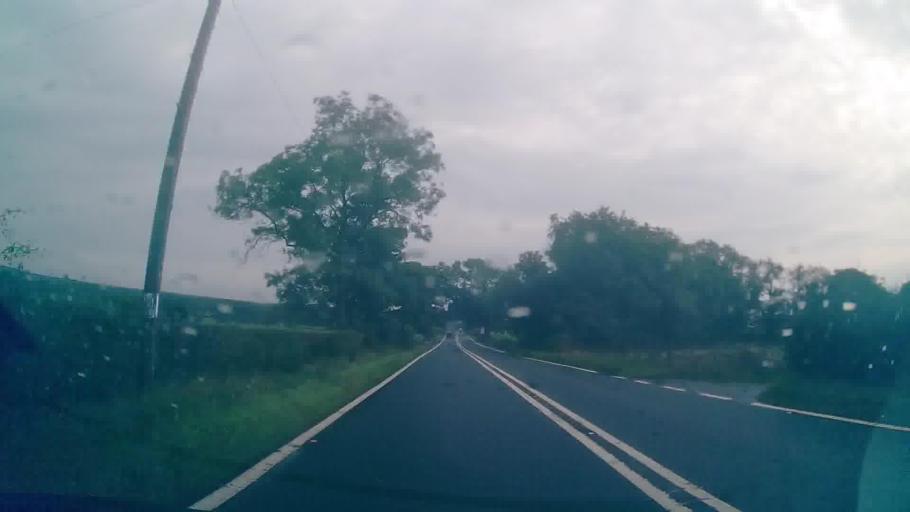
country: GB
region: Scotland
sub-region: Dumfries and Galloway
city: Lochmaben
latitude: 55.0632
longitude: -3.4966
